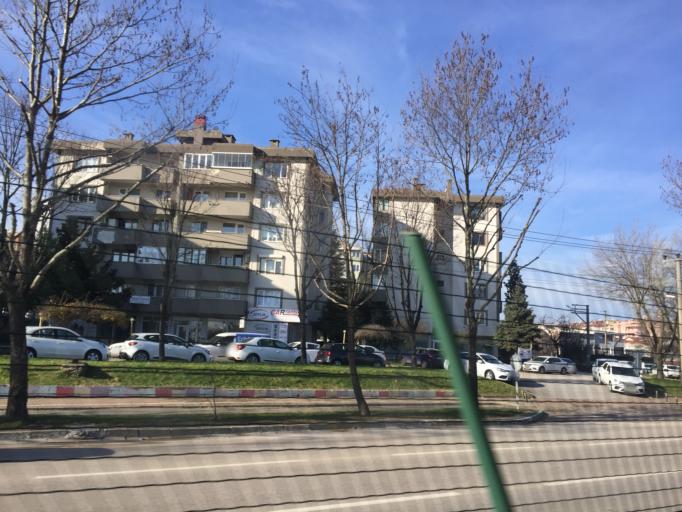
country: TR
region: Bursa
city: Yildirim
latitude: 40.2268
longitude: 28.9900
